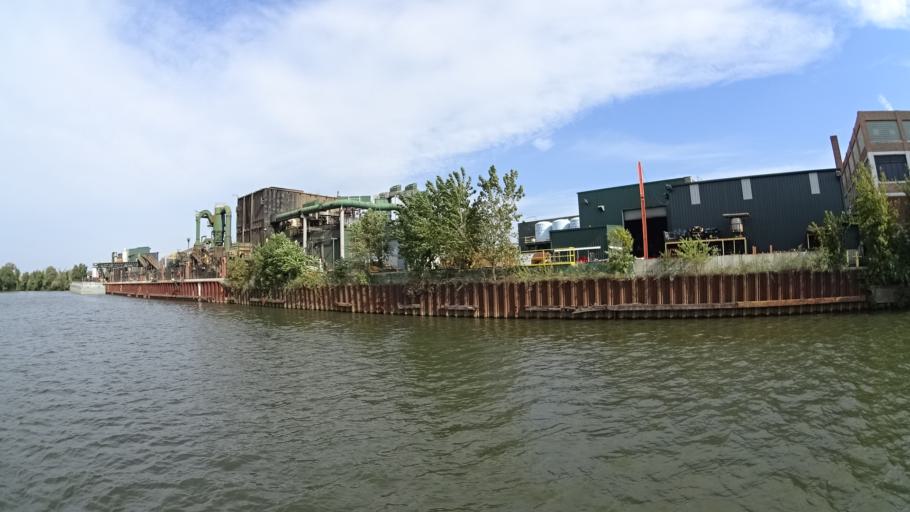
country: US
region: Illinois
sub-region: Cook County
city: Chicago
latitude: 41.9147
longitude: -87.6587
